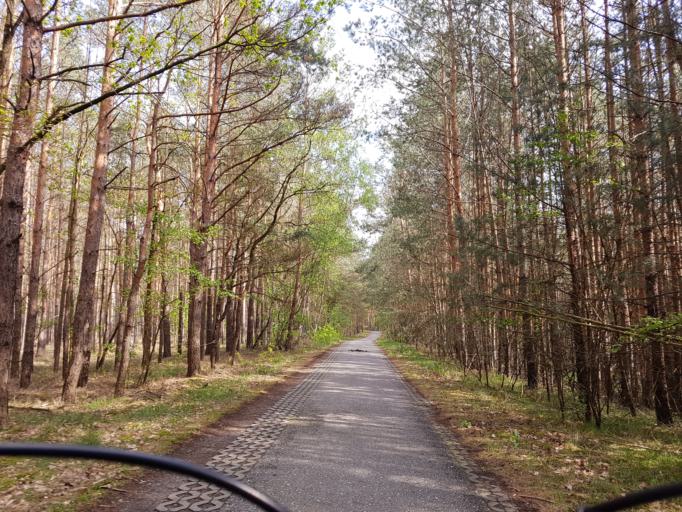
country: DE
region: Brandenburg
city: Schilda
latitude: 51.6050
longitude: 13.3606
